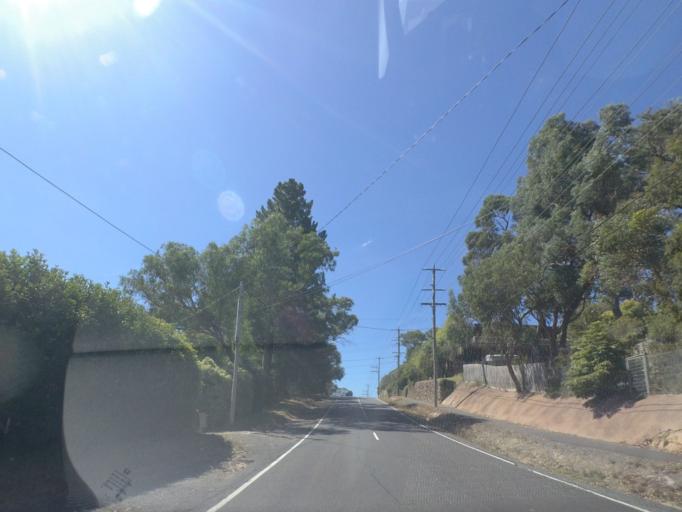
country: AU
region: Victoria
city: Mitcham
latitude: -37.8000
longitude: 145.2156
